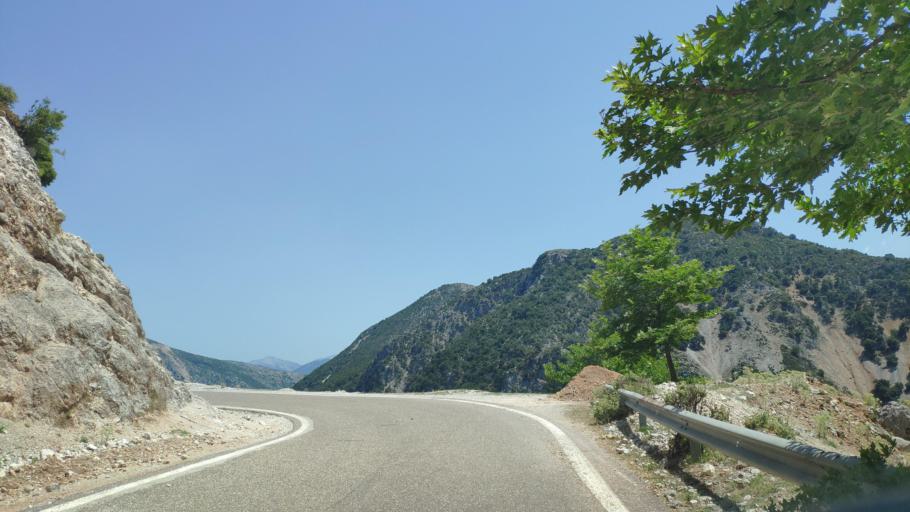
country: GR
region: West Greece
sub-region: Nomos Aitolias kai Akarnanias
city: Krikellos
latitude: 39.0129
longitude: 21.3728
